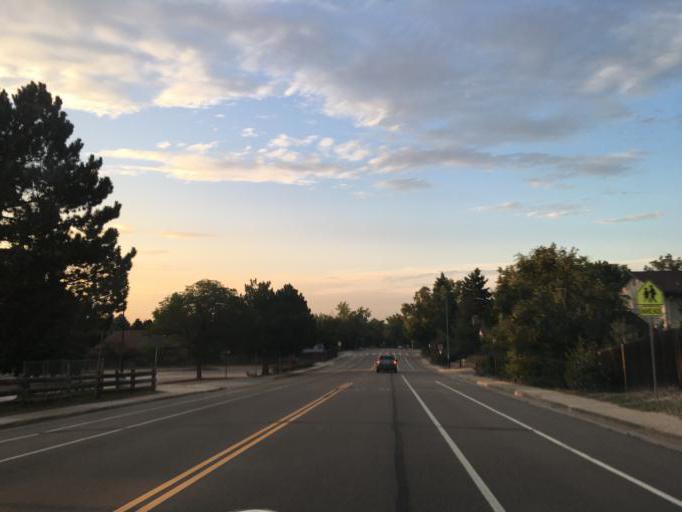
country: US
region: Colorado
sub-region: Adams County
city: Aurora
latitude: 39.6827
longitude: -104.8566
